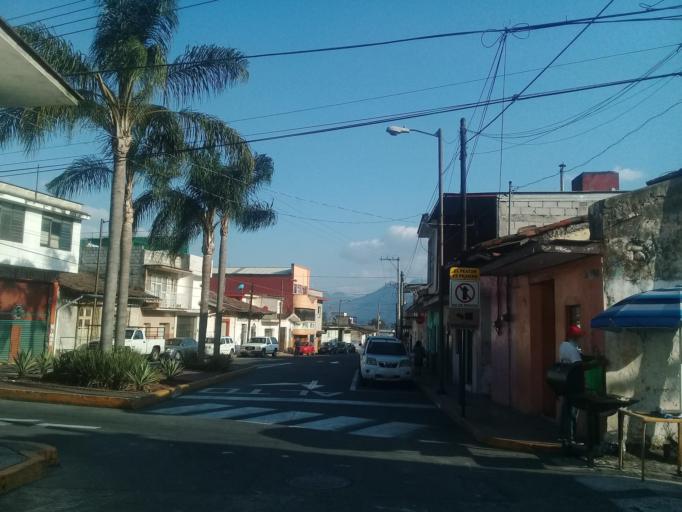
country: MX
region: Veracruz
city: Orizaba
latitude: 18.8549
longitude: -97.1101
